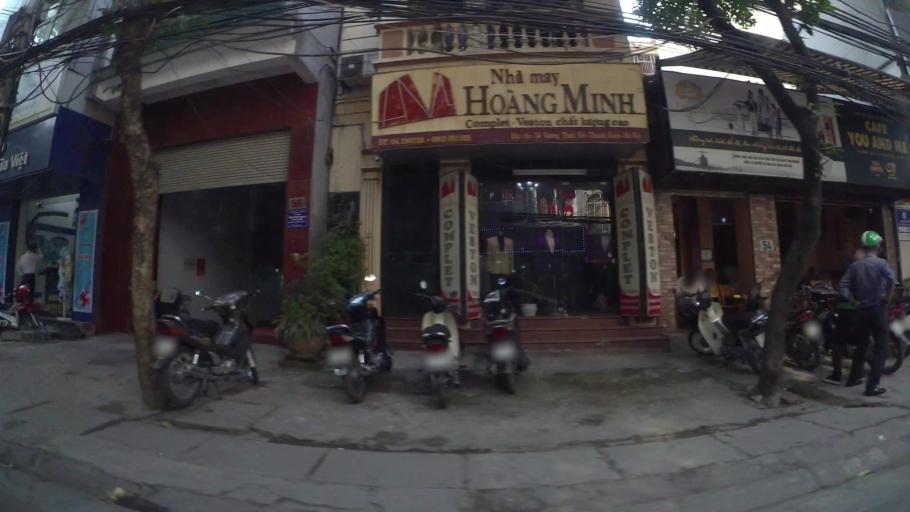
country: VN
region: Ha Noi
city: Dong Da
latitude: 20.9997
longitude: 105.8220
